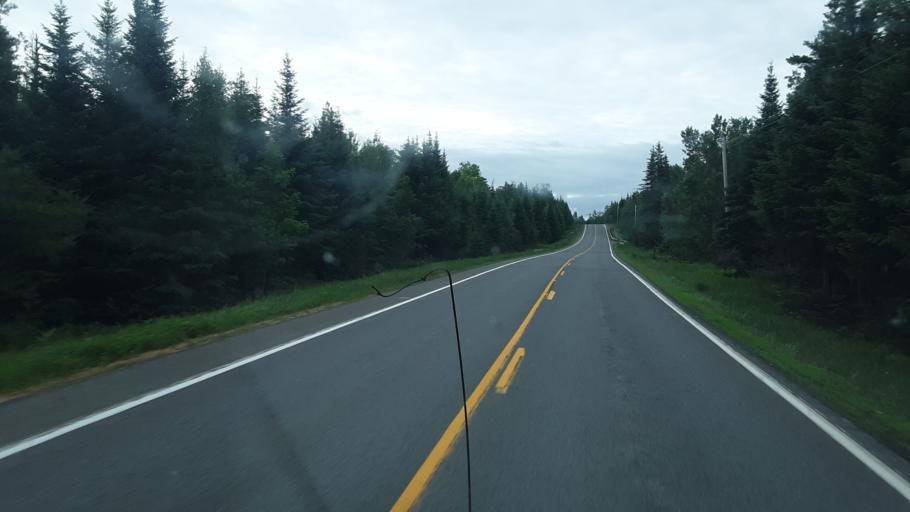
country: US
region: Maine
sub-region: Penobscot County
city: Patten
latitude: 46.4058
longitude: -68.3641
